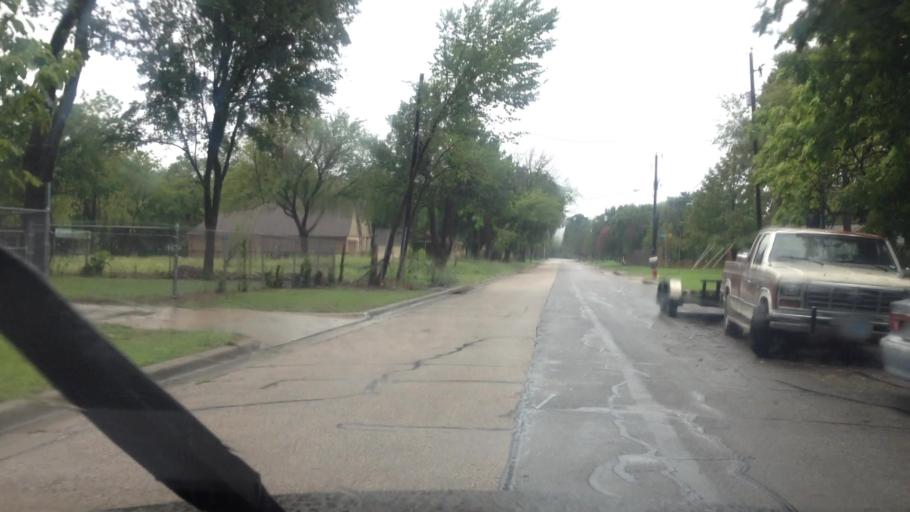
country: US
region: Texas
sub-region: Tarrant County
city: North Richland Hills
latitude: 32.8726
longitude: -97.2153
